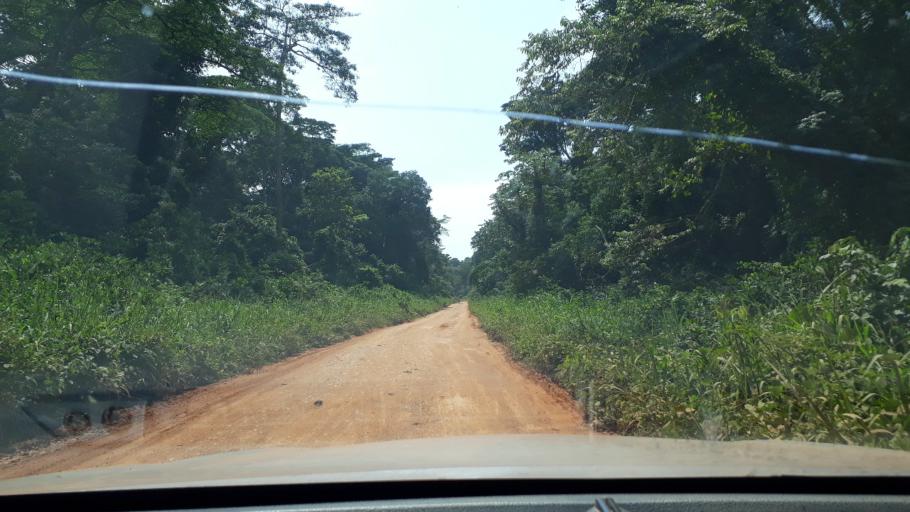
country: CD
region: Eastern Province
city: Wamba
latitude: 1.4237
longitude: 28.3608
